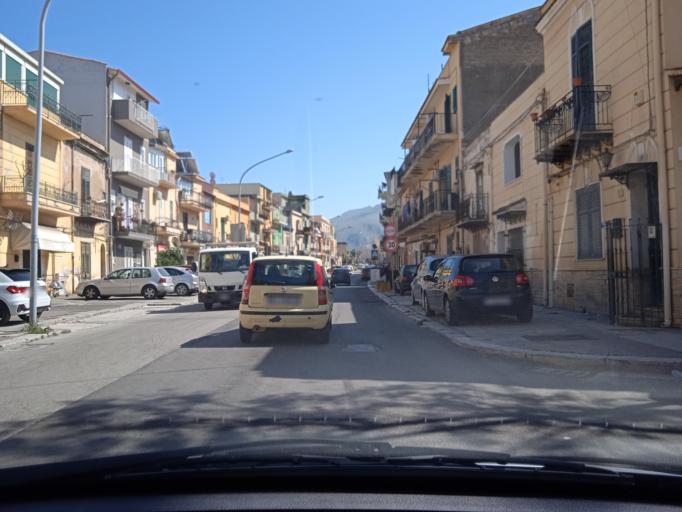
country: IT
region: Sicily
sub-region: Palermo
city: Villabate
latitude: 38.0951
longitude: 13.4296
